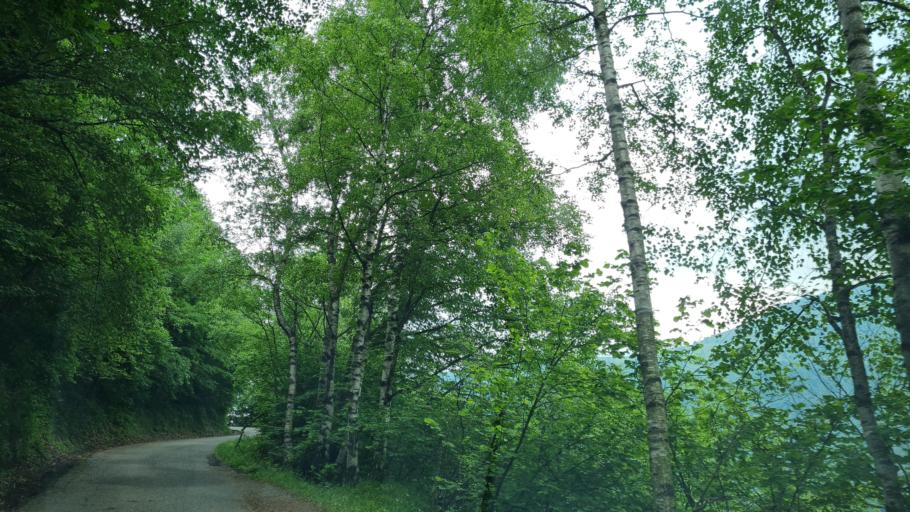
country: IT
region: Piedmont
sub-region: Provincia di Biella
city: Sordevolo
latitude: 45.5965
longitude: 7.9498
